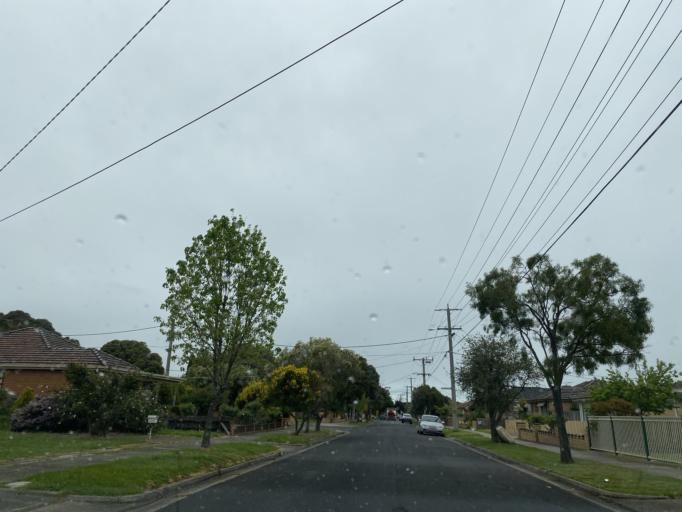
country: AU
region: Victoria
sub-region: Moreland
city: Fawkner
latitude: -37.7092
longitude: 144.9666
